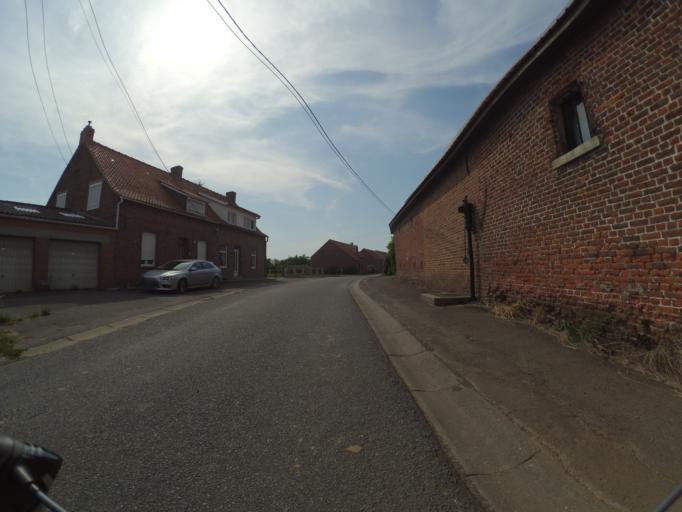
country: BE
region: Wallonia
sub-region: Province du Hainaut
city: Ellezelles
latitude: 50.7277
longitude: 3.6875
